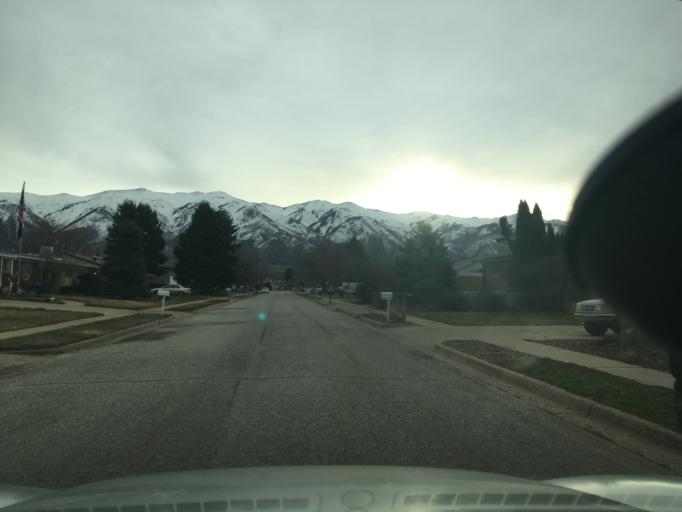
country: US
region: Utah
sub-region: Davis County
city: Layton
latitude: 41.0738
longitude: -111.9657
